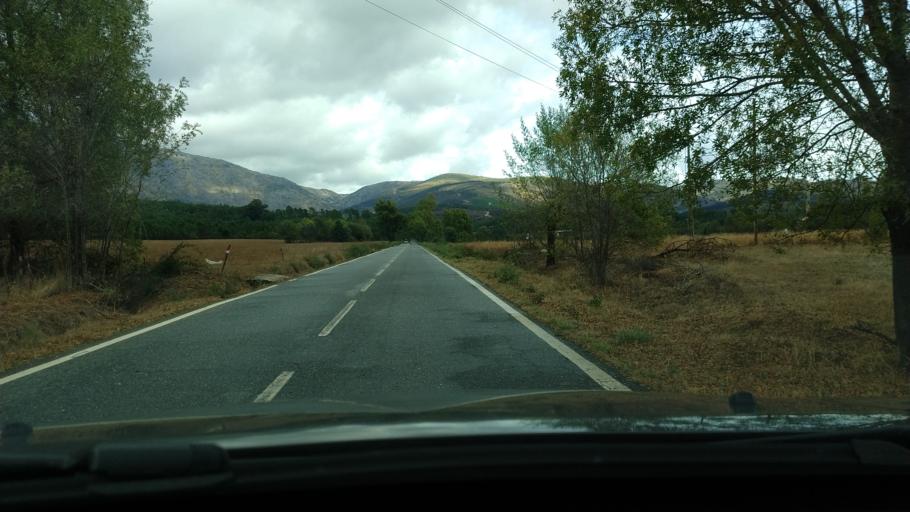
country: PT
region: Castelo Branco
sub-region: Covilha
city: Covilha
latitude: 40.2332
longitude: -7.6022
